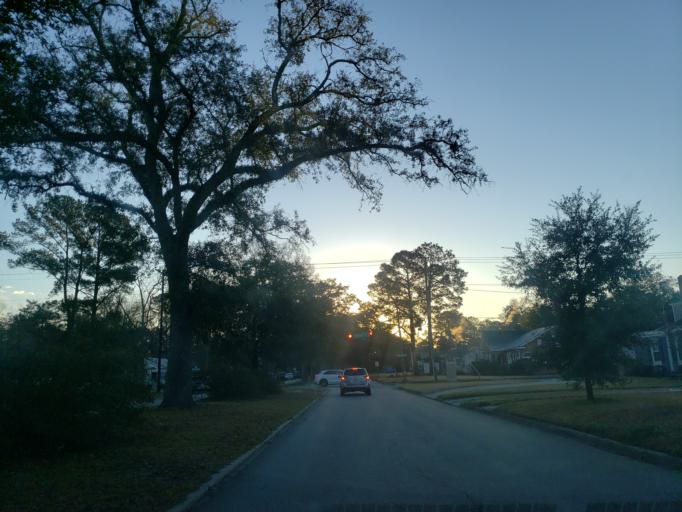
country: US
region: Georgia
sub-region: Chatham County
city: Savannah
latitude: 32.0378
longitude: -81.0986
